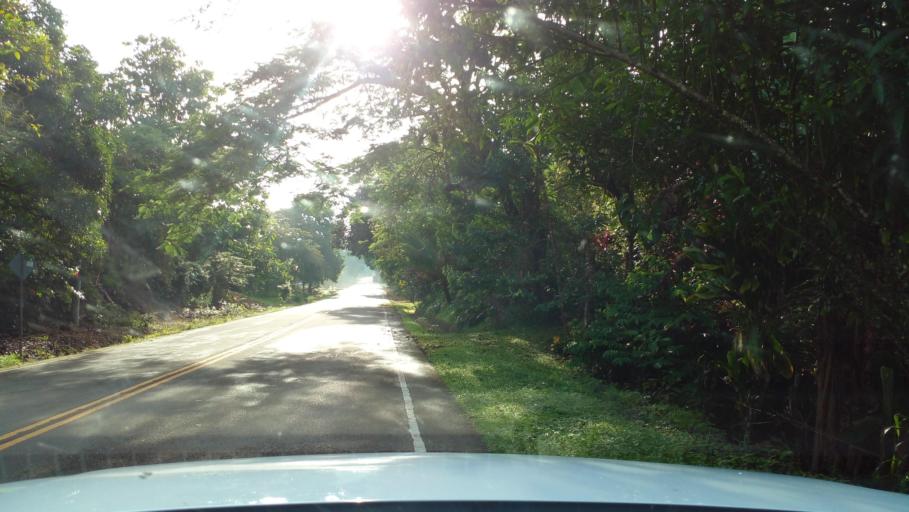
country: PA
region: Veraguas
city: Las Palmas
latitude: 8.0254
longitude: -81.4714
